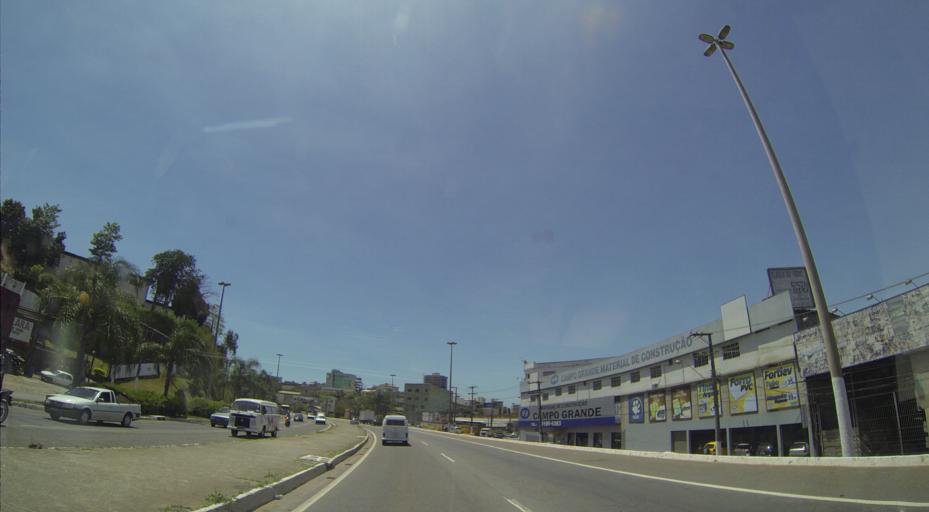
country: BR
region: Espirito Santo
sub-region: Vitoria
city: Vitoria
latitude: -20.3382
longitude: -40.3845
